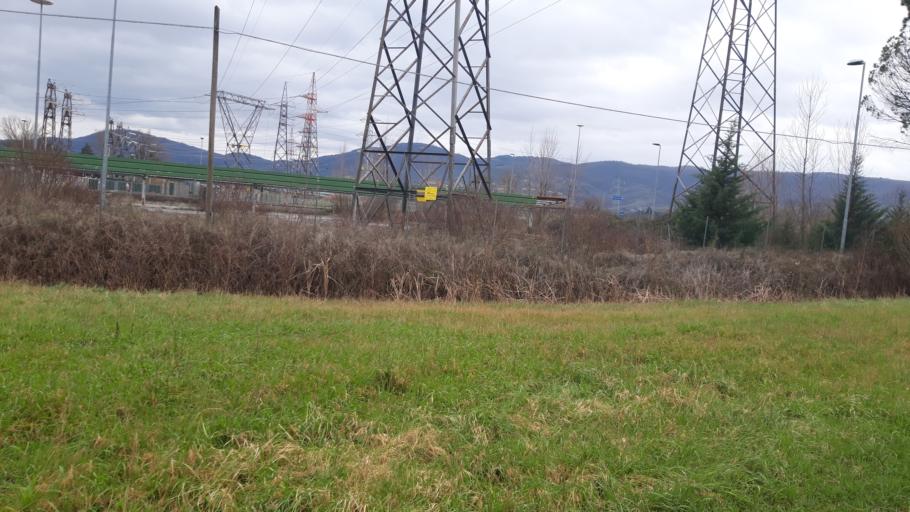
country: IT
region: Umbria
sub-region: Provincia di Perugia
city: Fontignano
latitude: 43.0059
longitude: 12.1798
